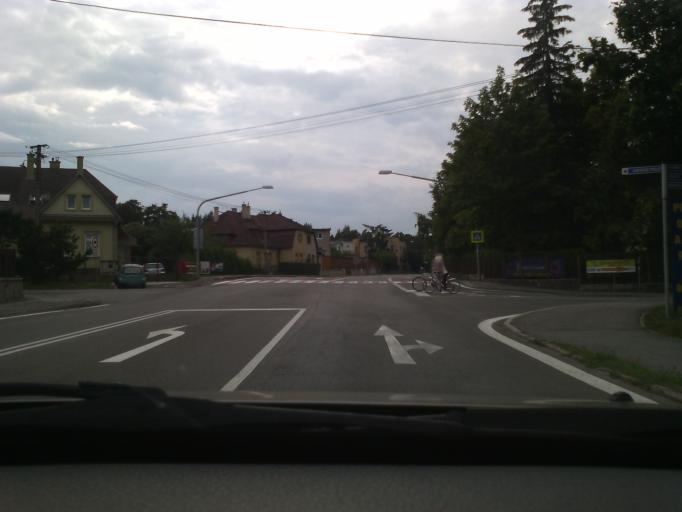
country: SK
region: Presovsky
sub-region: Okres Presov
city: Kezmarok
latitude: 49.1319
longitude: 20.4240
